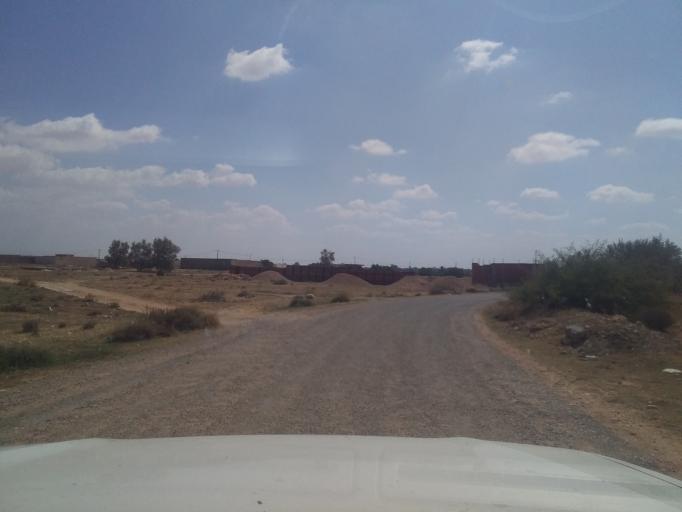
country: TN
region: Madanin
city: Medenine
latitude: 33.6119
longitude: 10.3043
